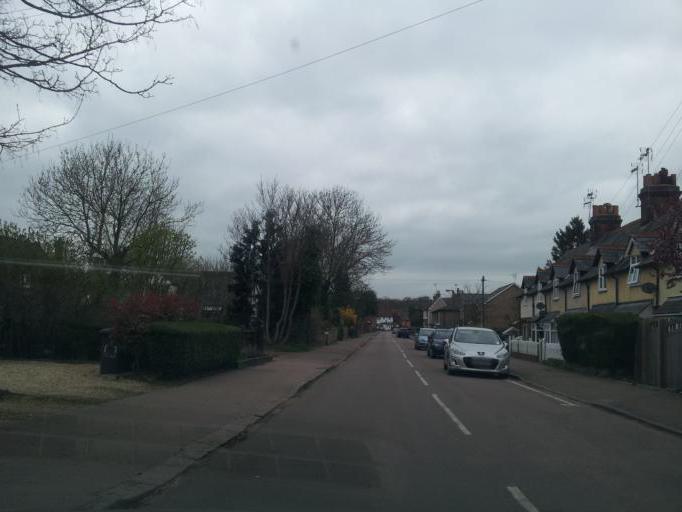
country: GB
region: England
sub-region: Hertfordshire
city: Great Munden
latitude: 51.8892
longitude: 0.0157
